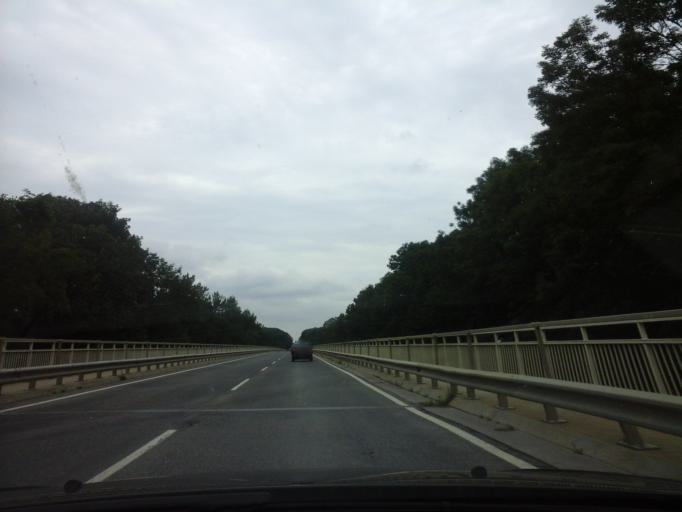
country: AT
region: Lower Austria
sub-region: Politischer Bezirk Bruck an der Leitha
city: Bad Deutsch-Altenburg
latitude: 48.1530
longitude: 16.9034
